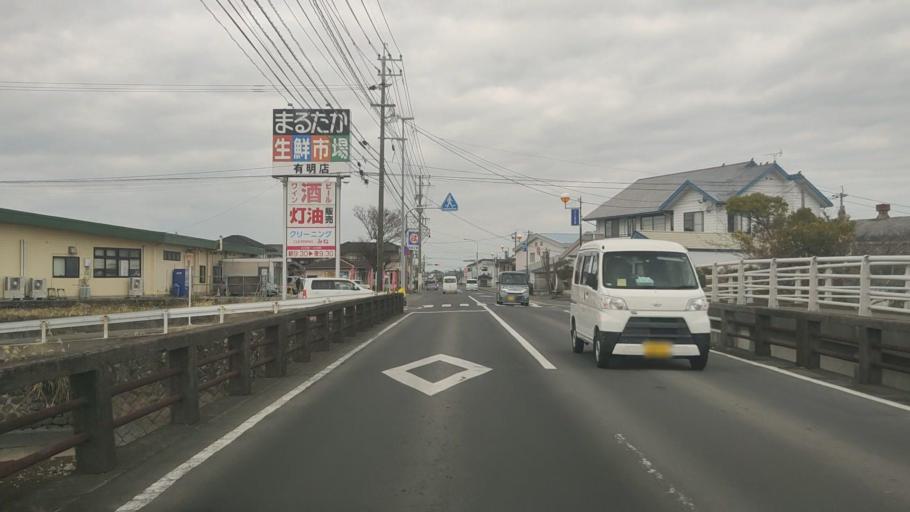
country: JP
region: Nagasaki
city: Shimabara
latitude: 32.8611
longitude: 130.3260
